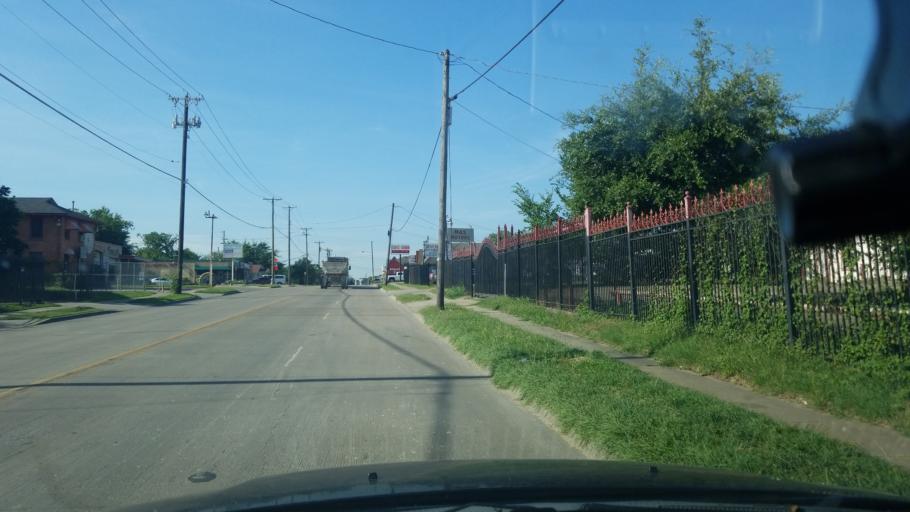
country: US
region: Texas
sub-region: Dallas County
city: Dallas
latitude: 32.7249
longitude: -96.8229
